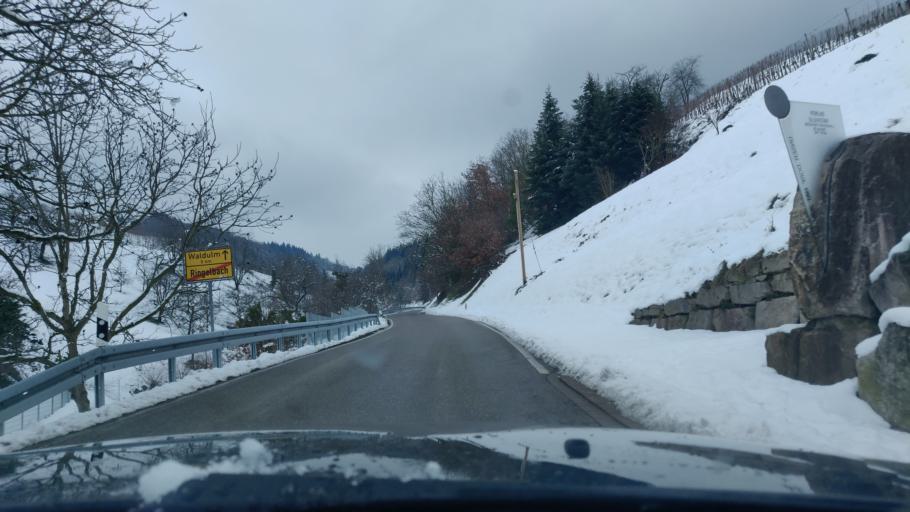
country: DE
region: Baden-Wuerttemberg
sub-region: Freiburg Region
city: Oberkirch
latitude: 48.5584
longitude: 8.0895
